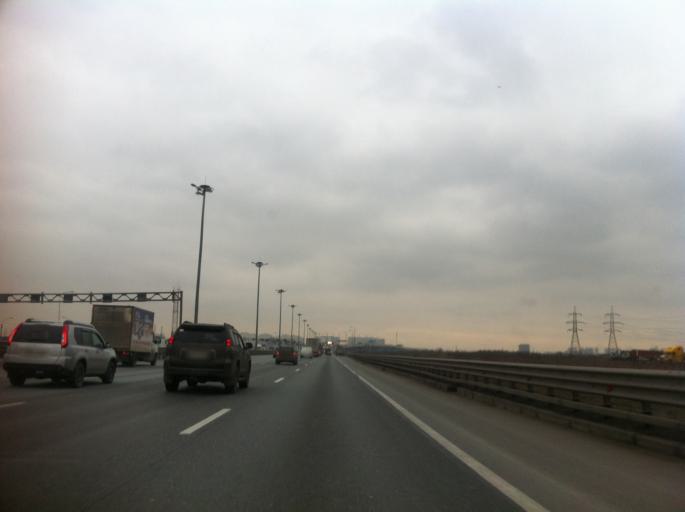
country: RU
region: St.-Petersburg
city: Obukhovo
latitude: 59.8223
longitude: 30.4199
